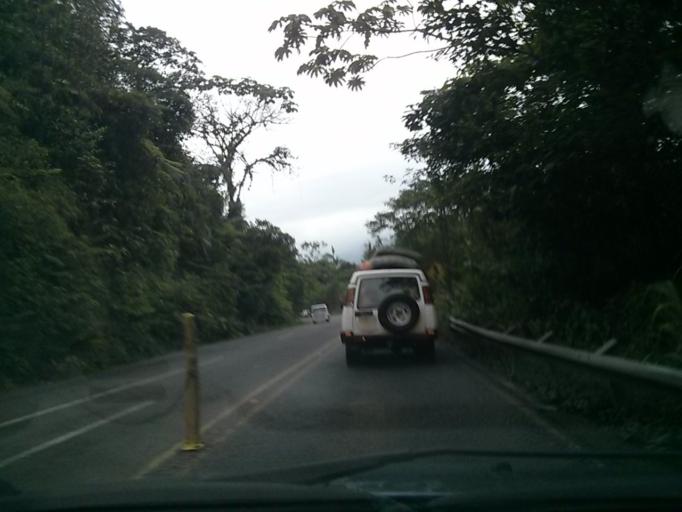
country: CR
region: San Jose
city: Dulce Nombre de Jesus
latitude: 10.1561
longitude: -83.9707
